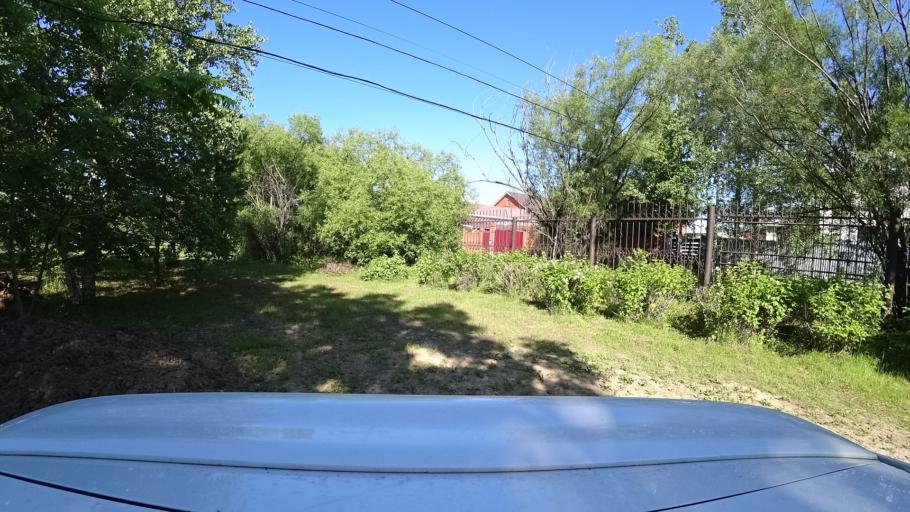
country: RU
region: Khabarovsk Krai
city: Topolevo
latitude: 48.5465
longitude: 135.1795
